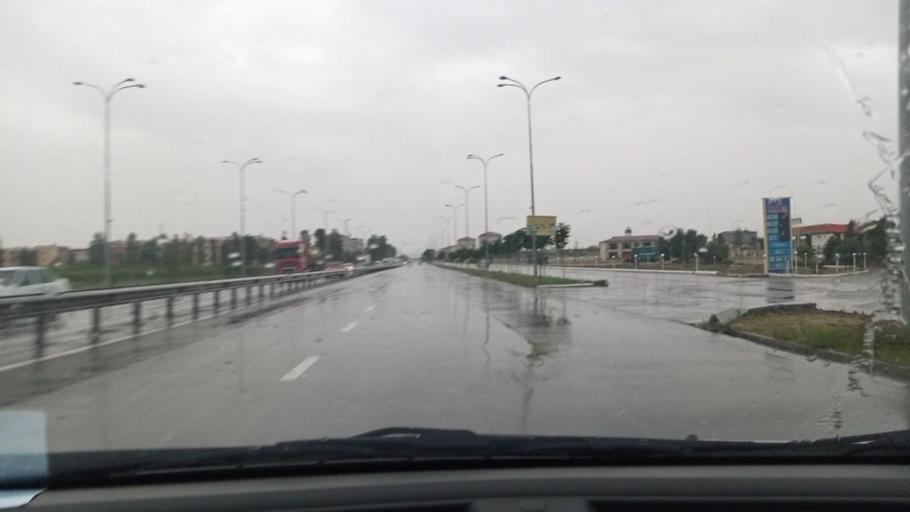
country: UZ
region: Toshkent
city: Ohangaron
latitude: 40.9117
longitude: 69.6169
